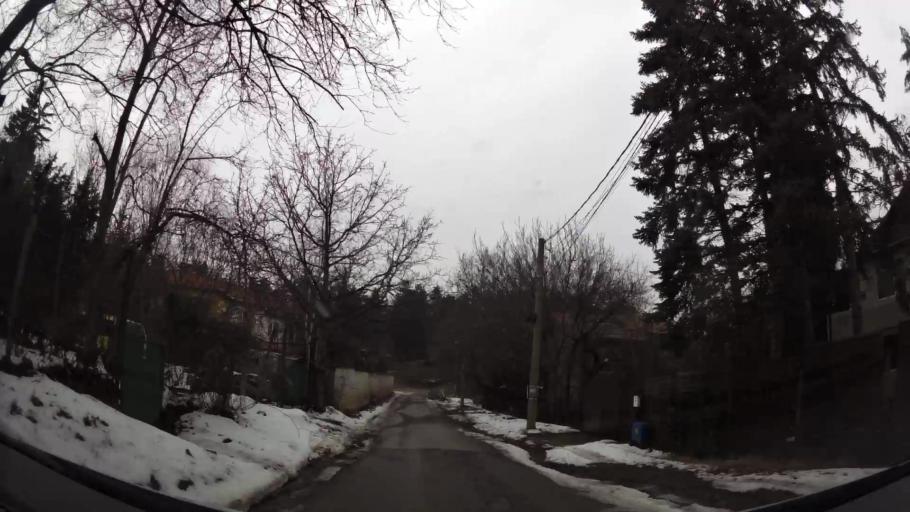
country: BG
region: Sofiya
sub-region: Obshtina Bozhurishte
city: Bozhurishte
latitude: 42.6730
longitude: 23.2286
